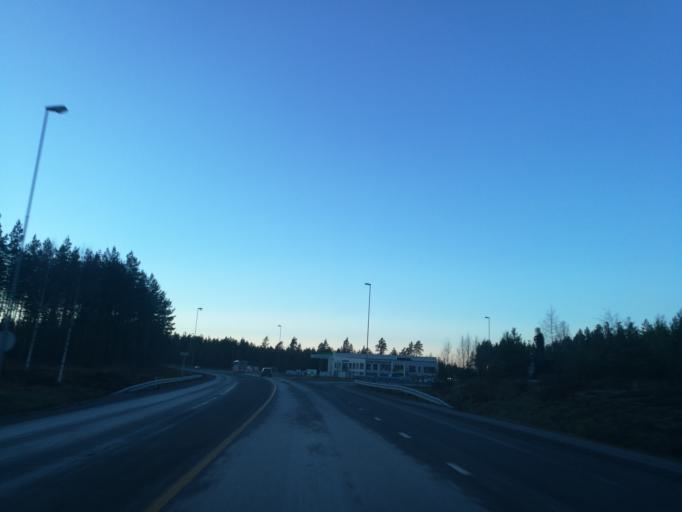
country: SE
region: Vaermland
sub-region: Eda Kommun
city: Charlottenberg
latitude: 59.9374
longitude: 12.2188
